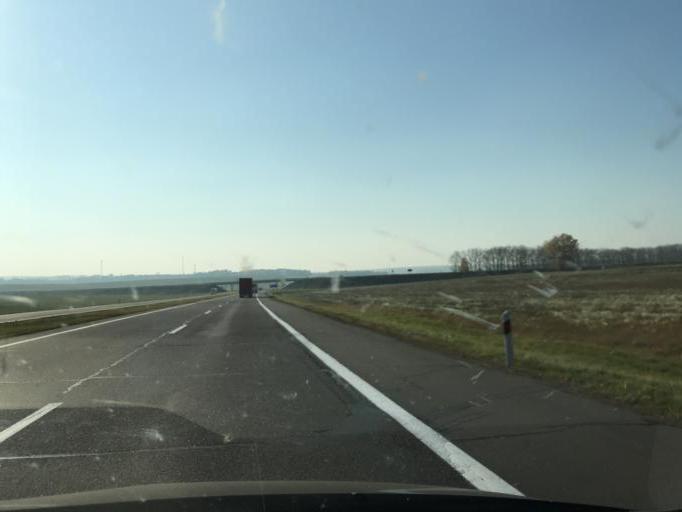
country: BY
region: Minsk
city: Snow
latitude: 53.2694
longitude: 26.2954
